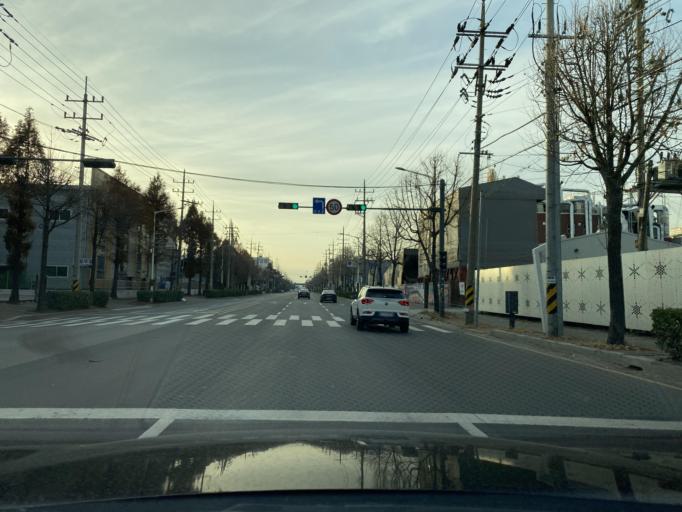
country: KR
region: Incheon
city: Incheon
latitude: 37.4992
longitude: 126.6579
